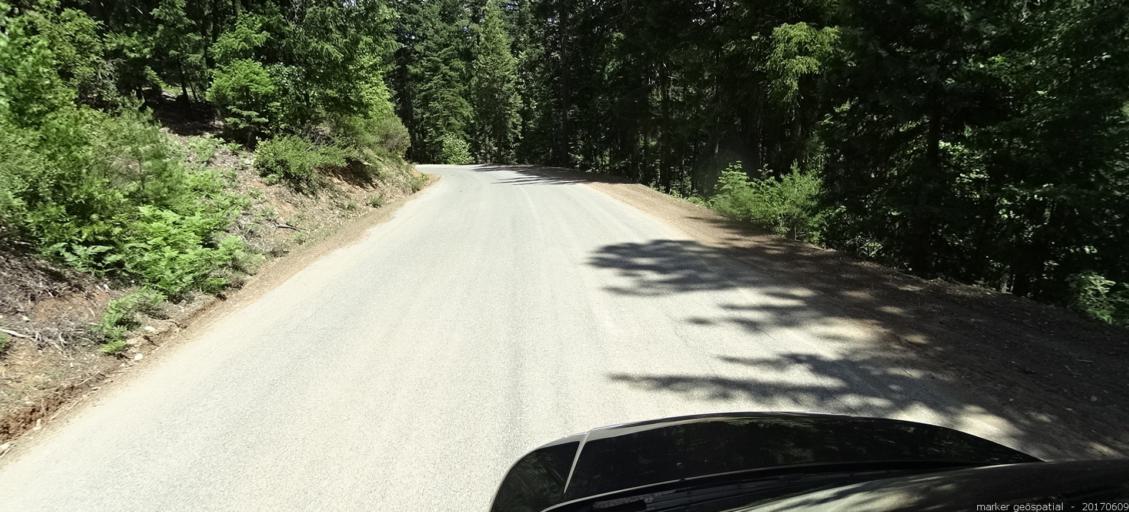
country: US
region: California
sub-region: Siskiyou County
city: Yreka
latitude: 41.4290
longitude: -122.9532
